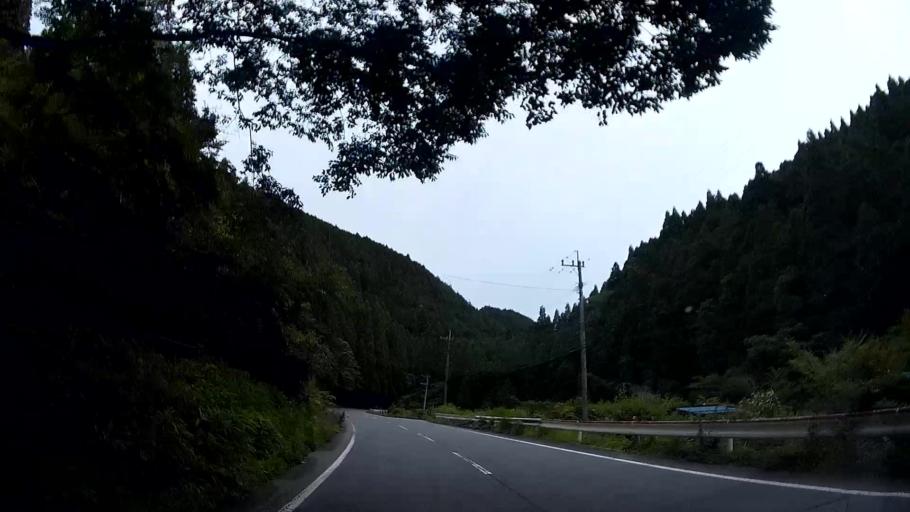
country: JP
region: Kumamoto
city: Kikuchi
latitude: 33.0484
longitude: 130.8960
